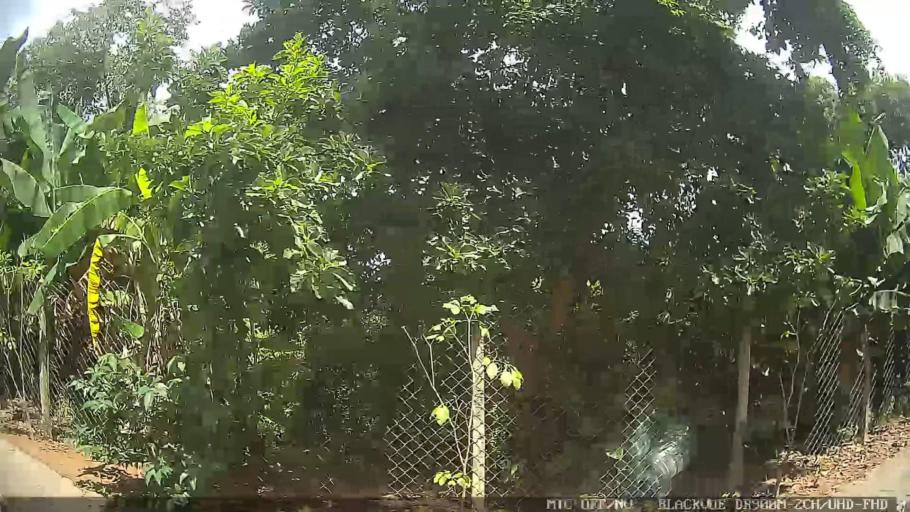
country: BR
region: Sao Paulo
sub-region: Atibaia
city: Atibaia
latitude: -23.1201
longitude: -46.6010
